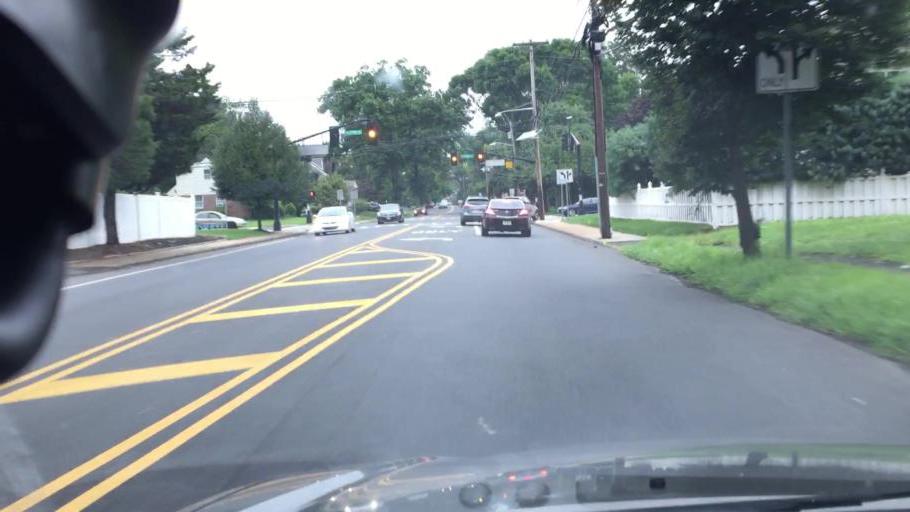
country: US
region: New Jersey
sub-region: Union County
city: Garwood
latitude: 40.6410
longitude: -74.3279
